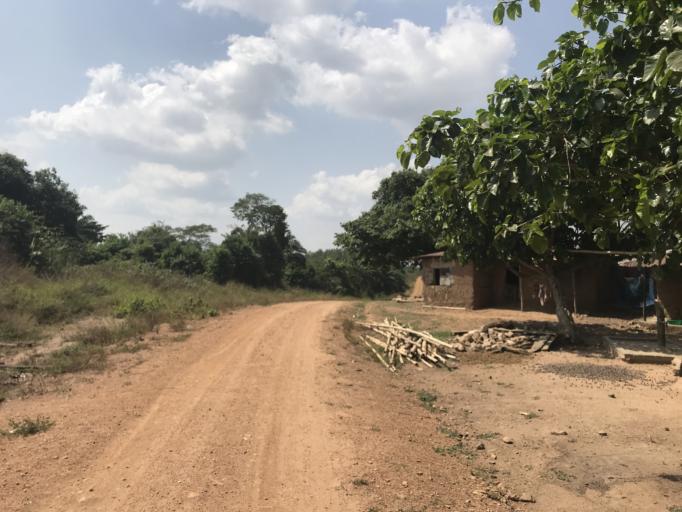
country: NG
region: Osun
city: Ifon
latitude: 7.9778
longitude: 4.5233
